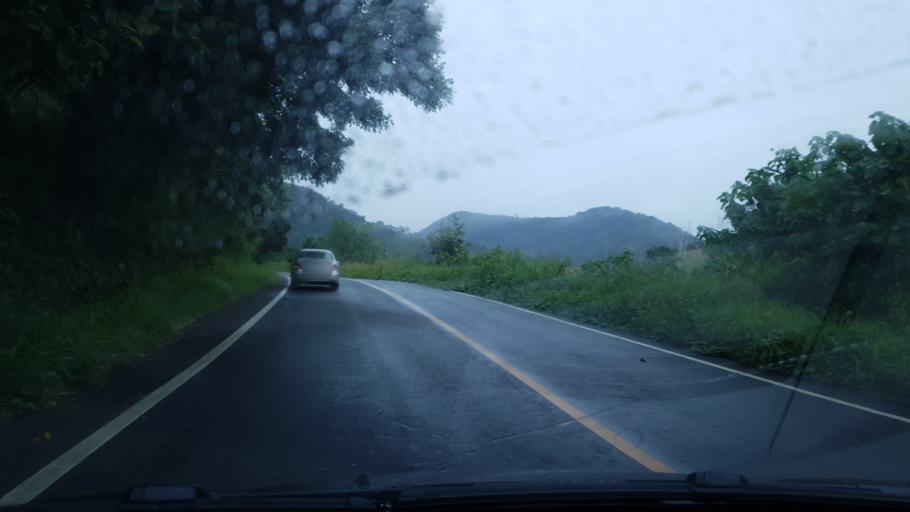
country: TH
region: Mae Hong Son
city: Khun Yuam
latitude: 18.6821
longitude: 97.9202
